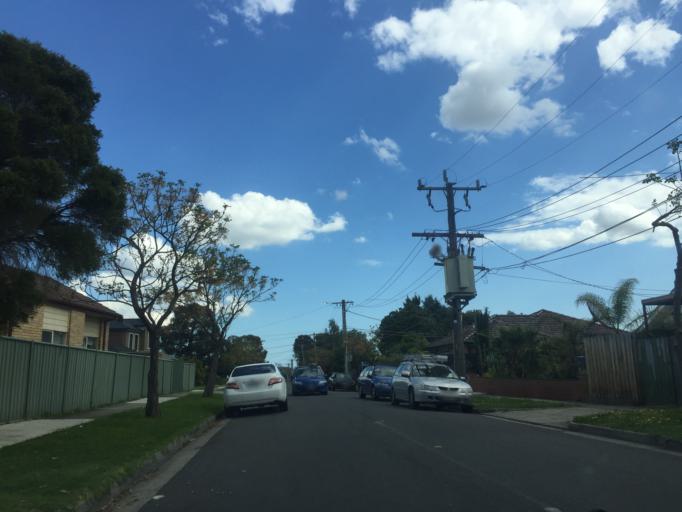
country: AU
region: Victoria
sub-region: Darebin
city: Kingsbury
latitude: -37.7145
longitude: 145.0387
